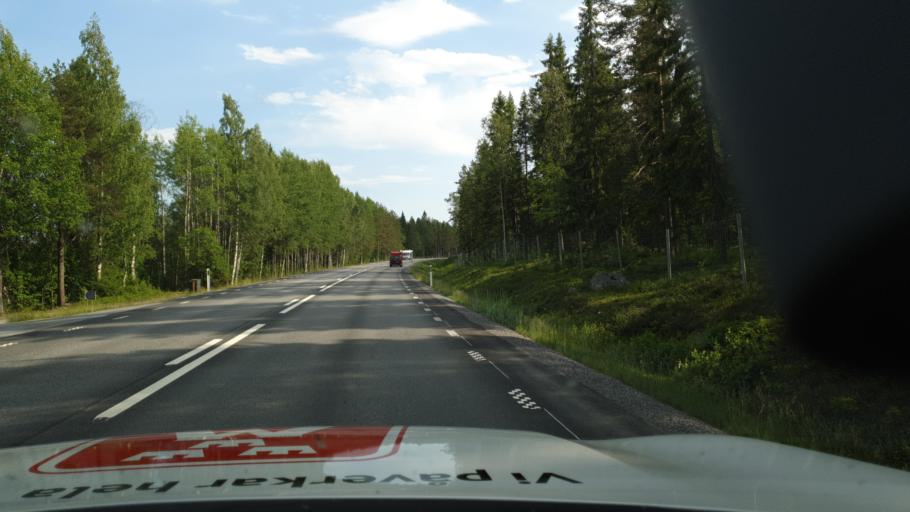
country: SE
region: Vaesterbotten
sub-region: Skelleftea Kommun
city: Burea
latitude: 64.5380
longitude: 21.2572
